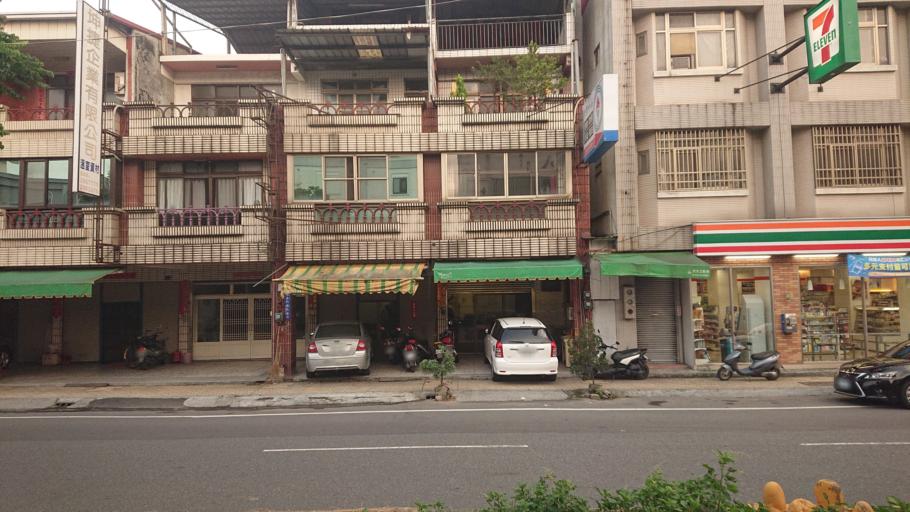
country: TW
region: Taiwan
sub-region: Nantou
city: Puli
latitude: 23.9733
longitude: 120.9698
